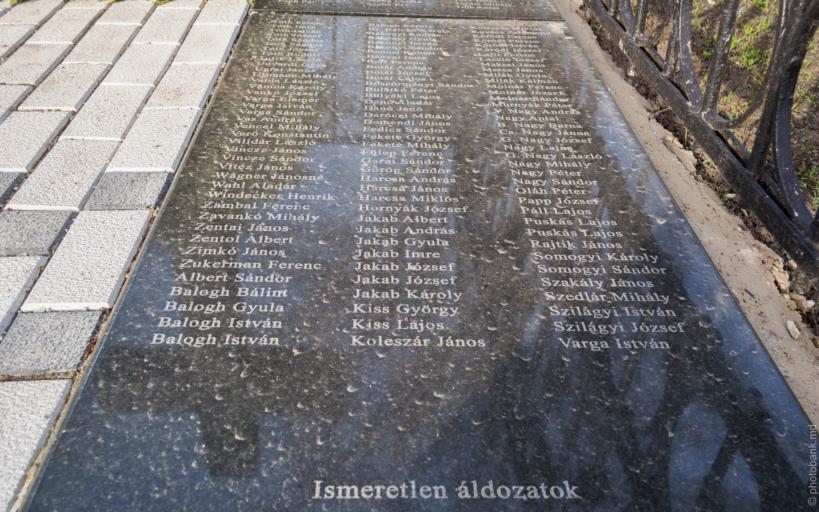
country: MD
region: Balti
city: Balti
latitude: 47.7703
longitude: 27.8974
